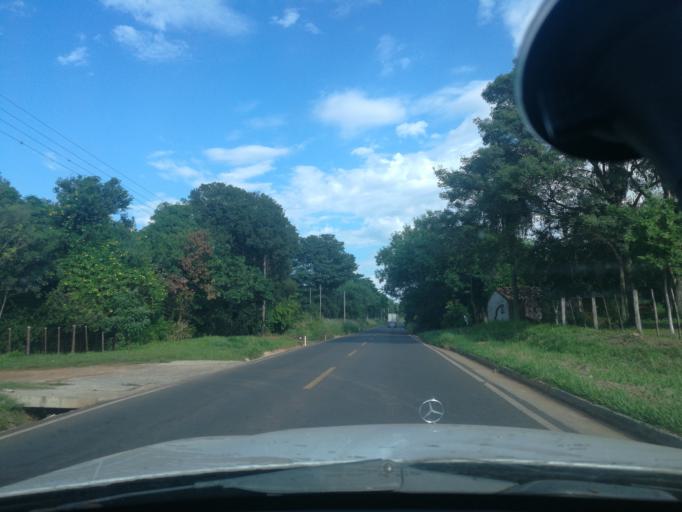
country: PY
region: Central
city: Capiata
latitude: -25.3142
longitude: -57.4612
